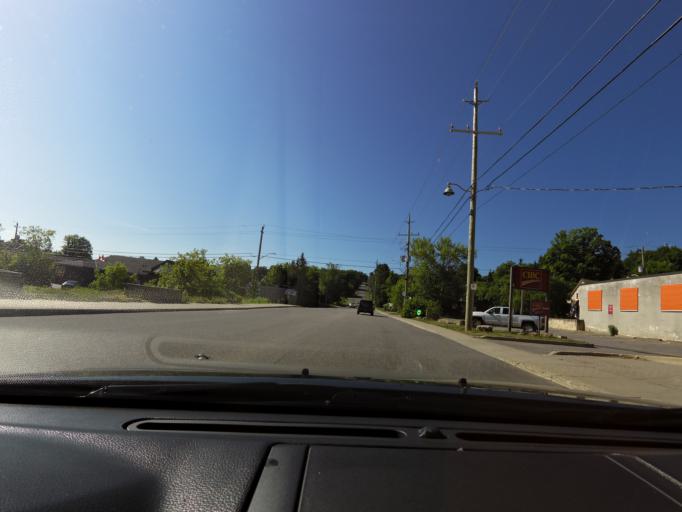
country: CA
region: Ontario
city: Huntsville
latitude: 45.3260
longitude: -79.2201
